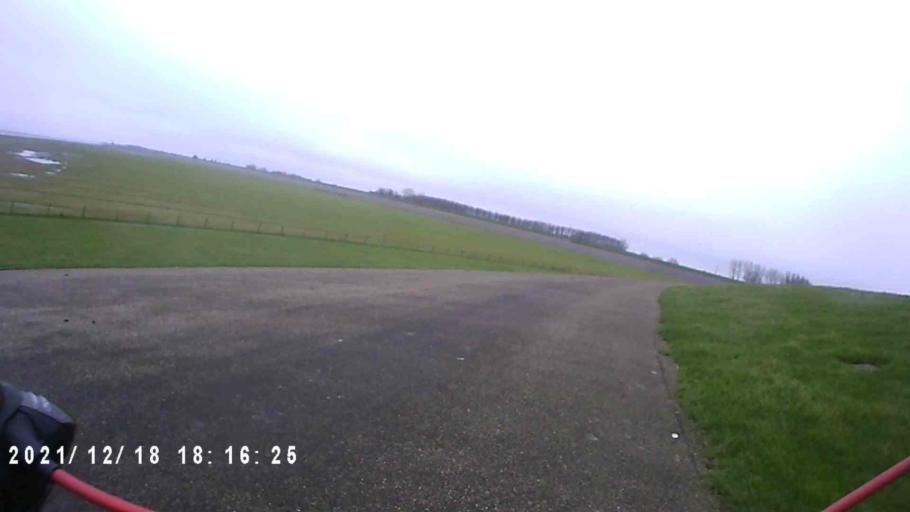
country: NL
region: Friesland
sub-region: Gemeente Dongeradeel
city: Ternaard
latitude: 53.3942
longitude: 5.9694
